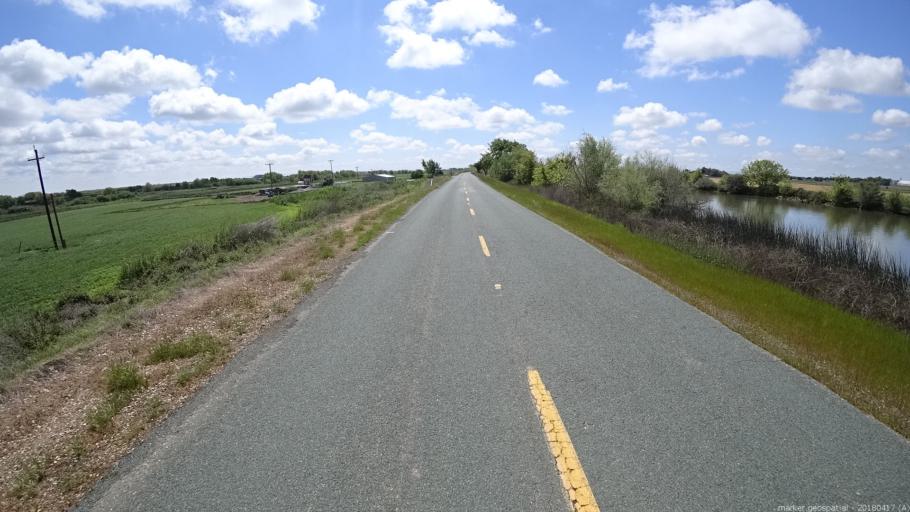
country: US
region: California
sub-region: Sacramento County
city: Walnut Grove
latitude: 38.1714
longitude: -121.5797
